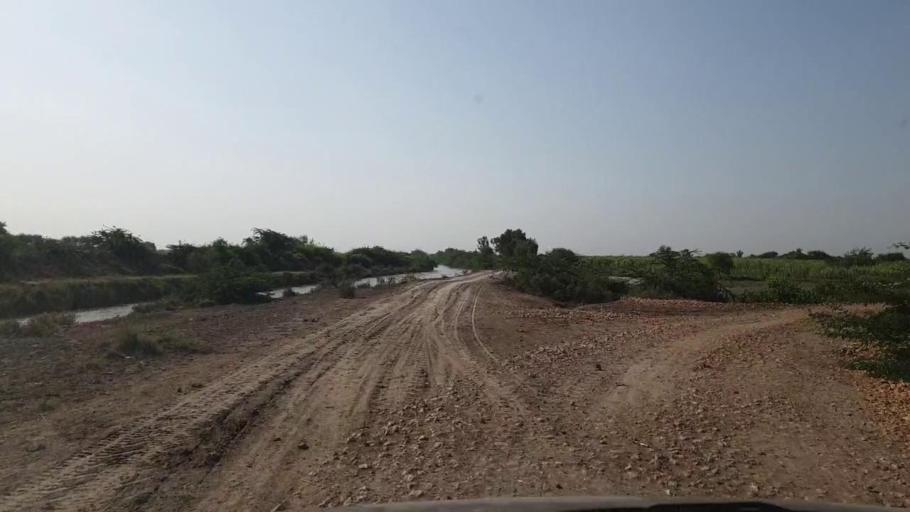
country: PK
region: Sindh
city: Kadhan
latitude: 24.6193
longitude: 69.0733
